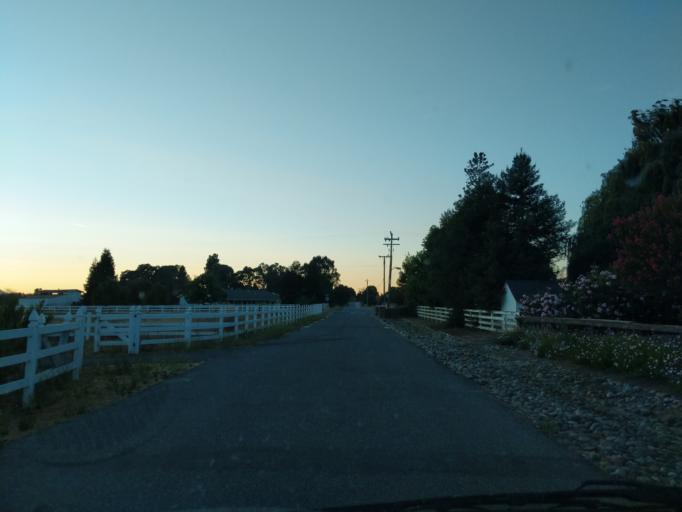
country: US
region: California
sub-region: Santa Clara County
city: Gilroy
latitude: 37.0610
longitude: -121.5578
